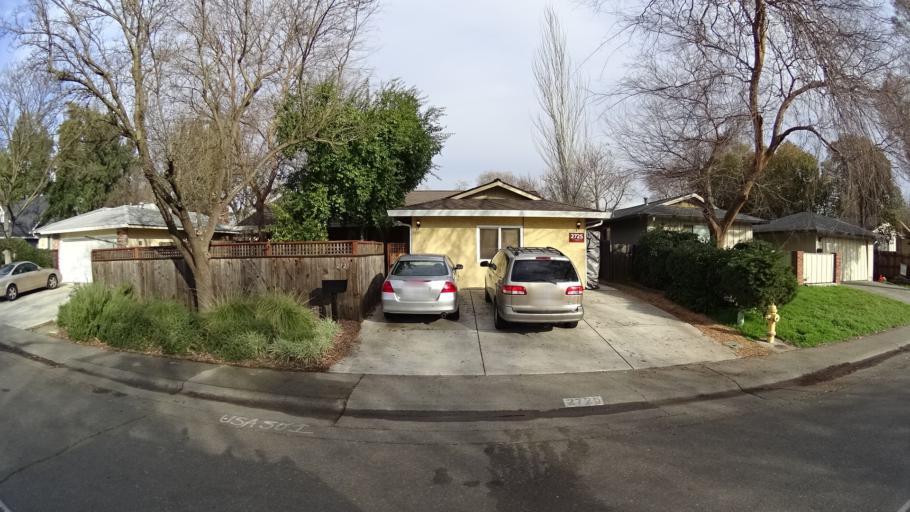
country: US
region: California
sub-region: Yolo County
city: Davis
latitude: 38.5579
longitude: -121.7185
